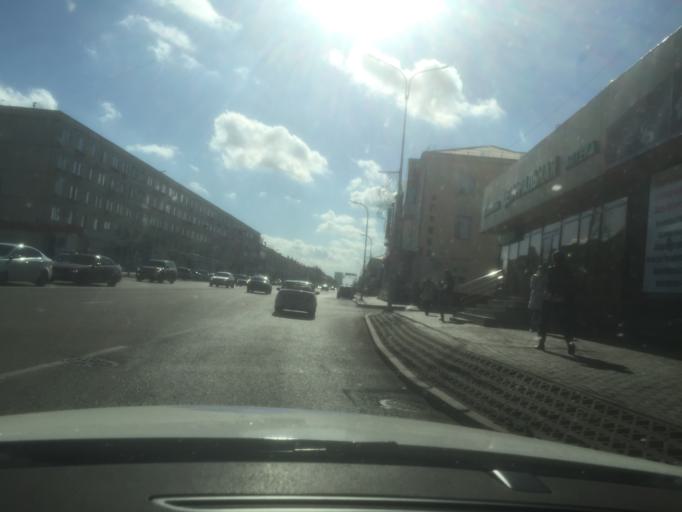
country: KZ
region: Astana Qalasy
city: Astana
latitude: 51.1885
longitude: 71.4148
